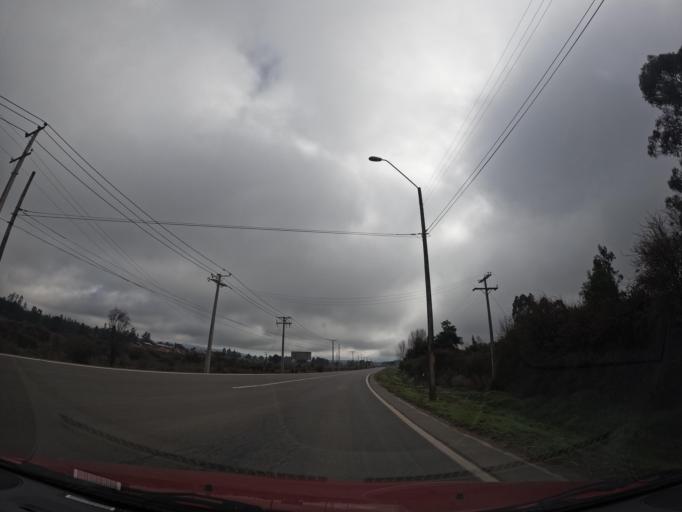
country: CL
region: Maule
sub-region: Provincia de Cauquenes
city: Cauquenes
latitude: -36.2706
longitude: -72.5458
